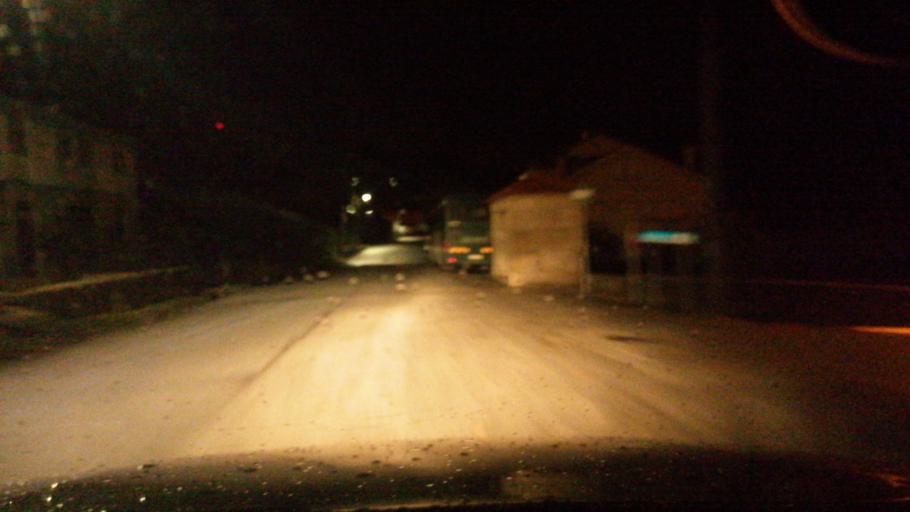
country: PT
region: Viseu
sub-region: Moimenta da Beira
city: Moimenta da Beira
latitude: 41.0411
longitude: -7.6400
